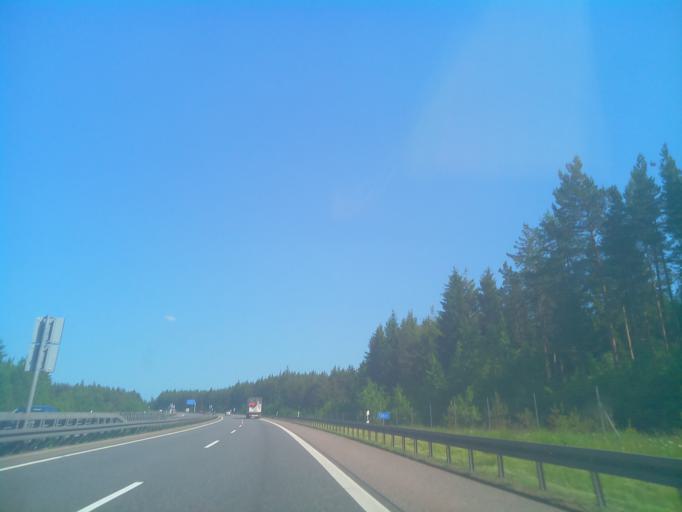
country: DE
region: Thuringia
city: Martinroda
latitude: 50.7126
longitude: 10.8828
